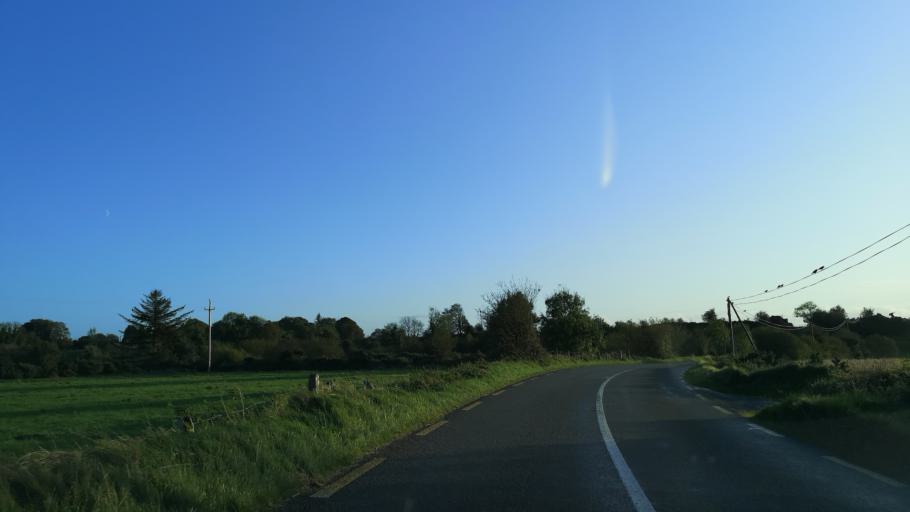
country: IE
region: Connaught
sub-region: Roscommon
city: Castlerea
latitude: 53.7032
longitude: -8.5663
